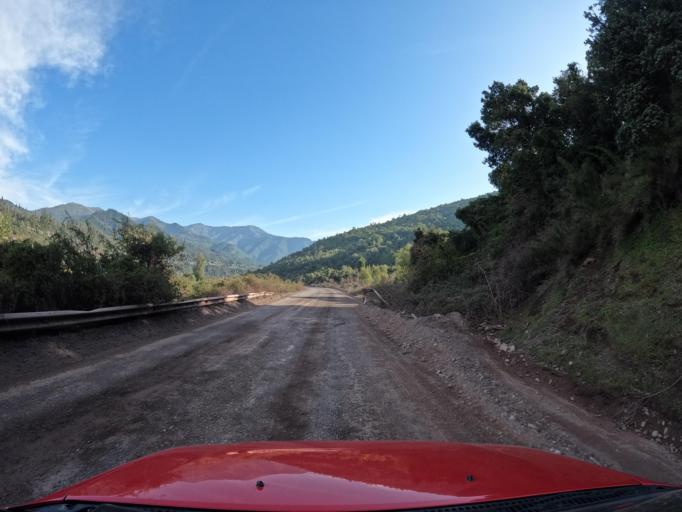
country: CL
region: O'Higgins
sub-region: Provincia de Colchagua
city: Chimbarongo
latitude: -34.9976
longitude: -70.8245
